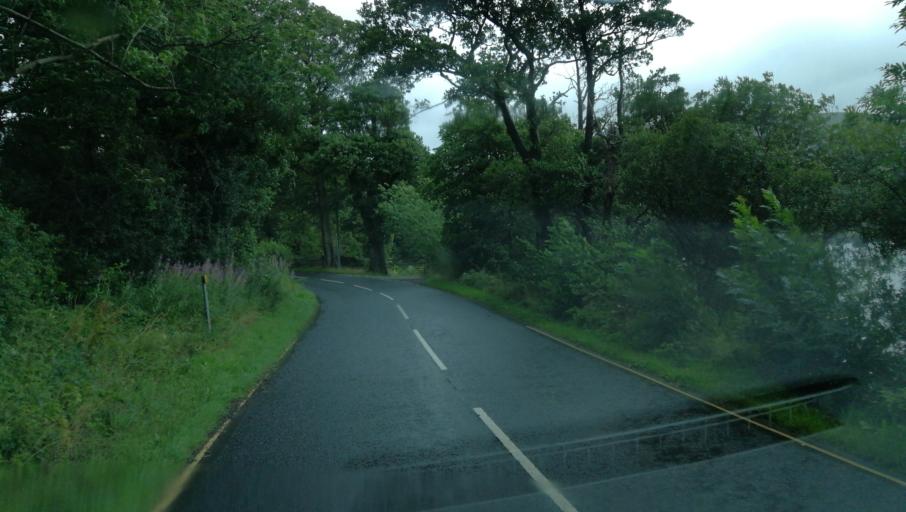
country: GB
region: England
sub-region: Cumbria
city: Penrith
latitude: 54.5819
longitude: -2.8780
